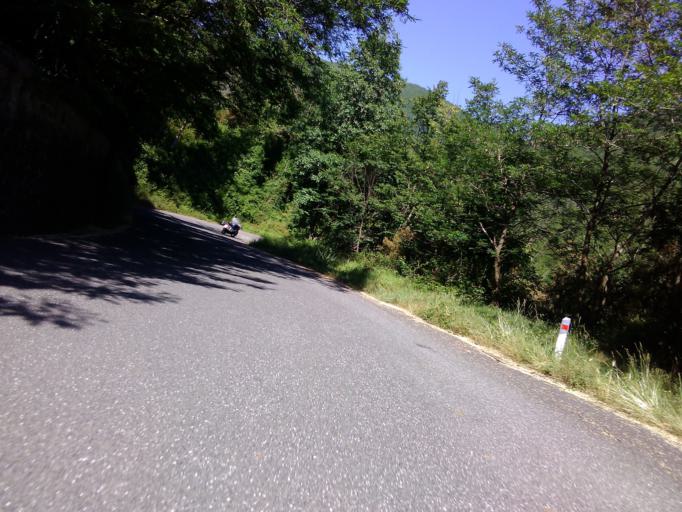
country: IT
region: Tuscany
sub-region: Provincia di Massa-Carrara
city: Comano
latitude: 44.3070
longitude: 10.0819
